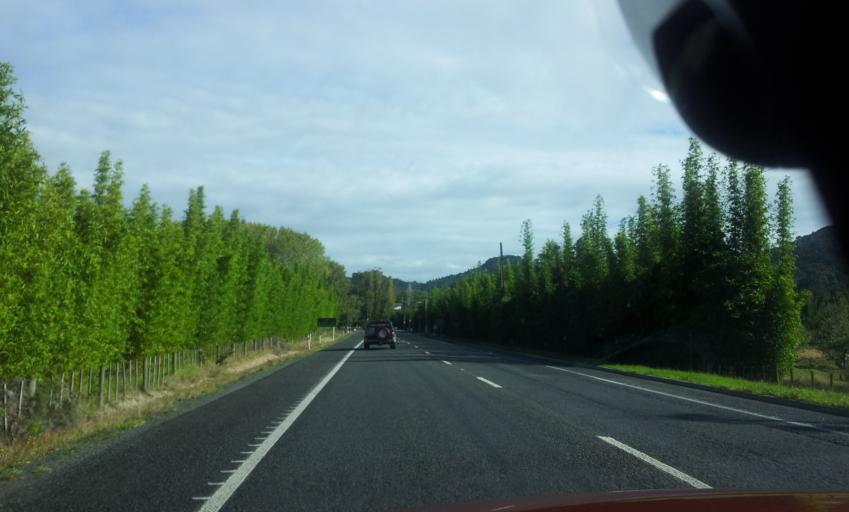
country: NZ
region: Auckland
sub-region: Auckland
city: Warkworth
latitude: -36.3828
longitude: 174.6385
